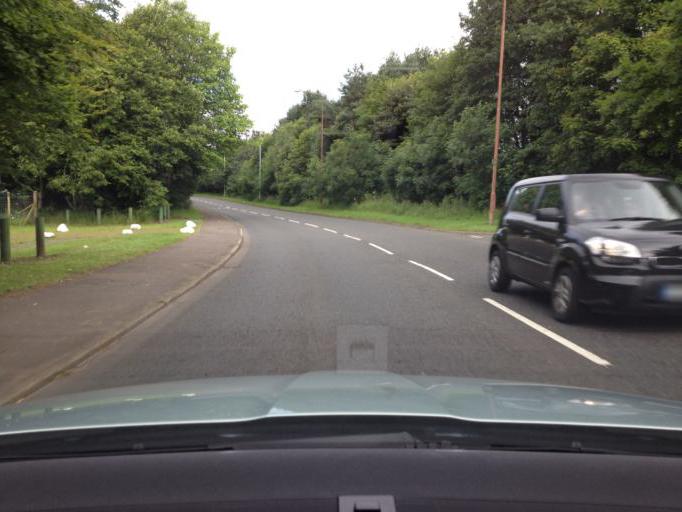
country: GB
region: Scotland
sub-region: West Lothian
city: Livingston
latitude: 55.8818
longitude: -3.5408
